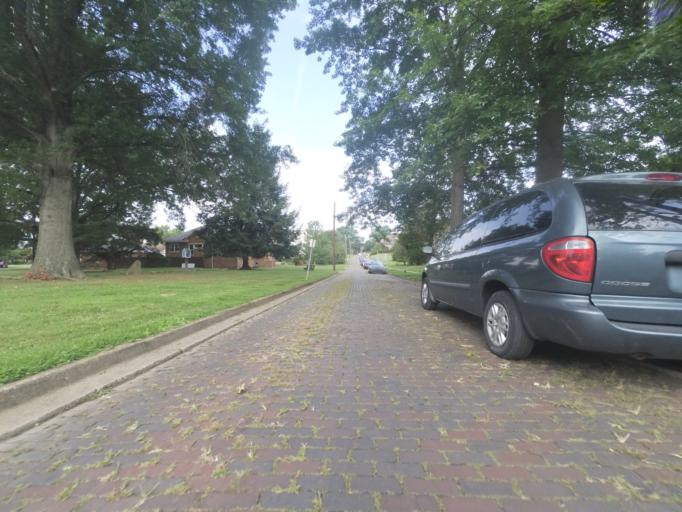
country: US
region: West Virginia
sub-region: Cabell County
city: Huntington
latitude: 38.4314
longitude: -82.3970
